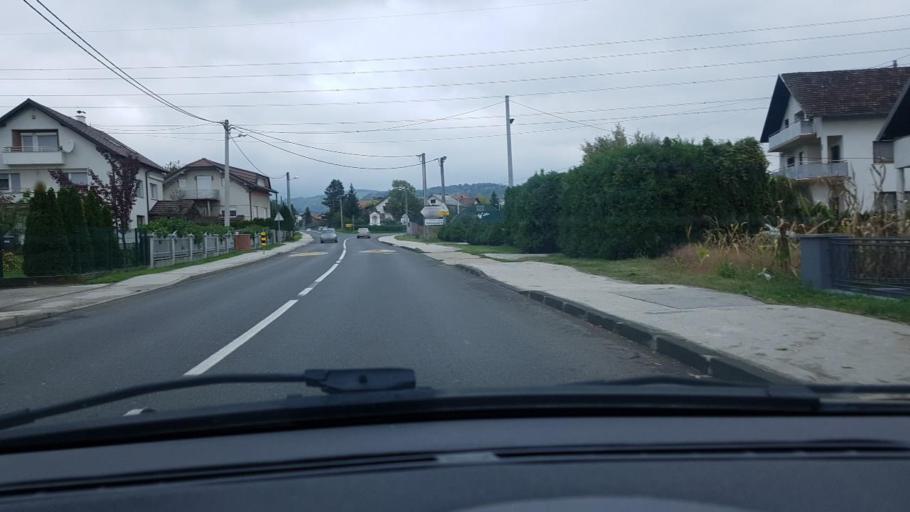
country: HR
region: Grad Zagreb
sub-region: Sesvete
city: Sesvete
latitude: 45.8708
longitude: 16.1133
